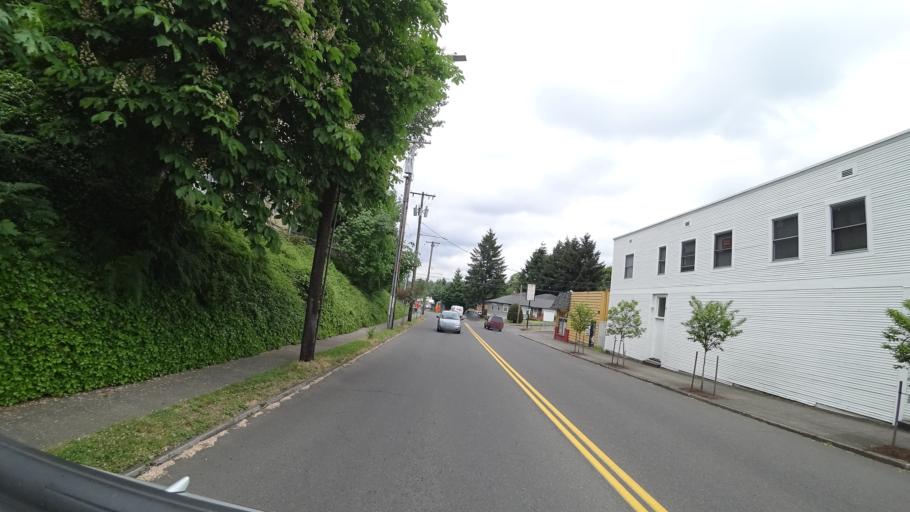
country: US
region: Oregon
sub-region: Multnomah County
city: Lents
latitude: 45.5011
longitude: -122.6113
